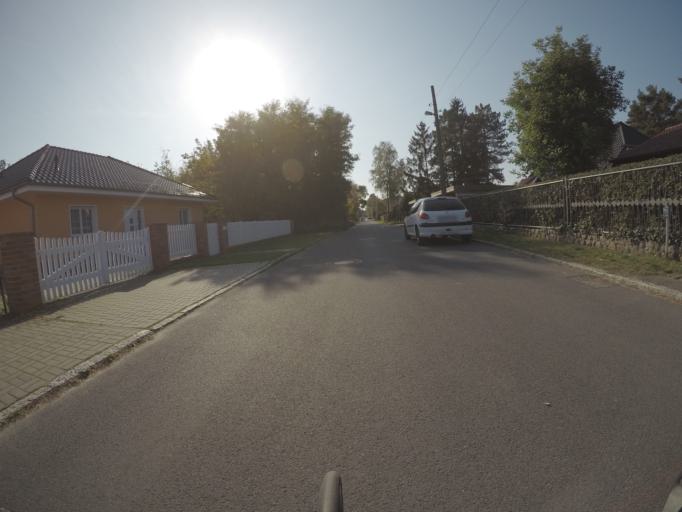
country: DE
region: Brandenburg
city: Oranienburg
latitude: 52.7363
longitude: 13.2531
